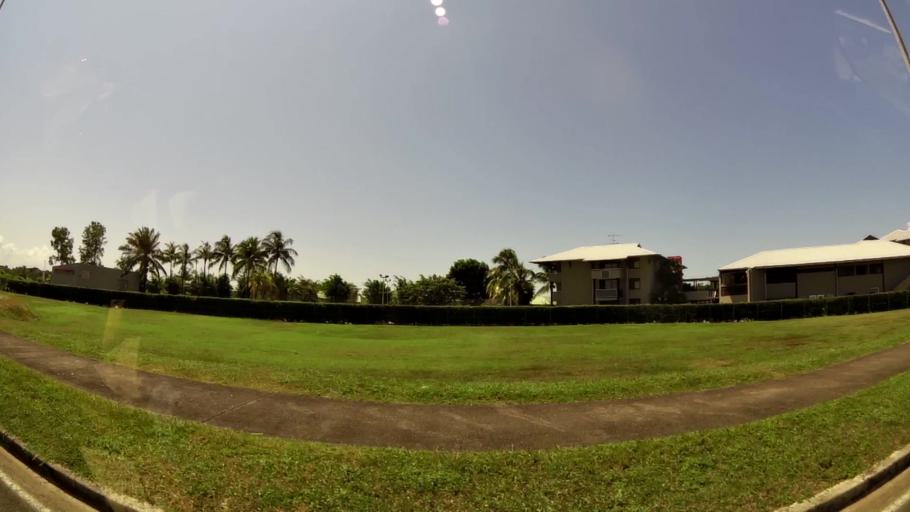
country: GF
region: Guyane
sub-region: Guyane
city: Kourou
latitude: 5.1727
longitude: -52.6577
